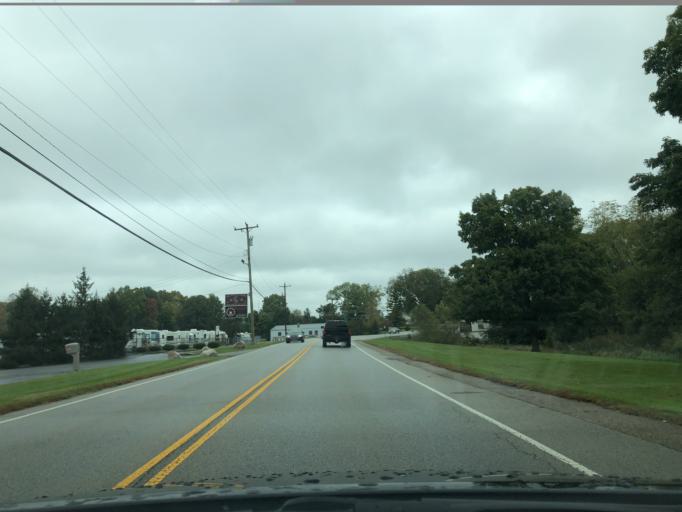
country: US
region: Ohio
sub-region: Hamilton County
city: Sharonville
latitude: 39.2767
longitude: -84.4098
